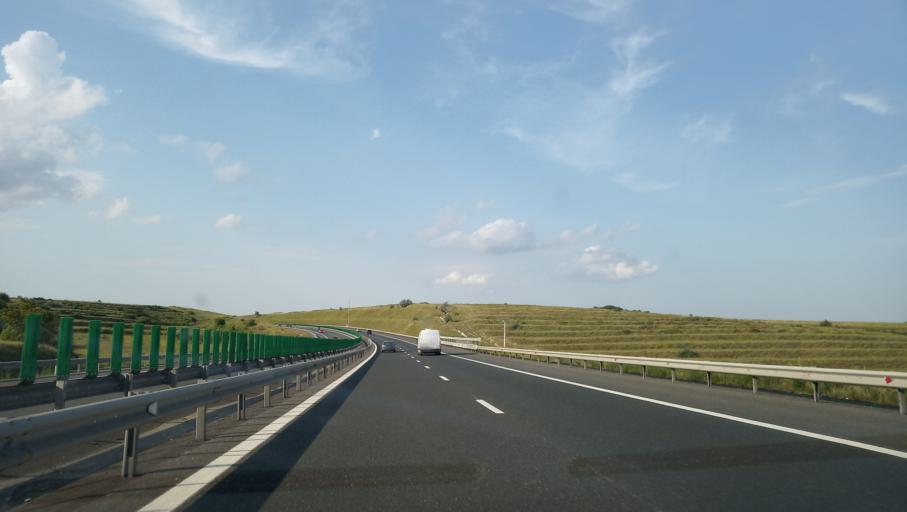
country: RO
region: Constanta
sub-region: Oras Cernavoda
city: Cernavoda
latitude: 44.3043
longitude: 28.0370
